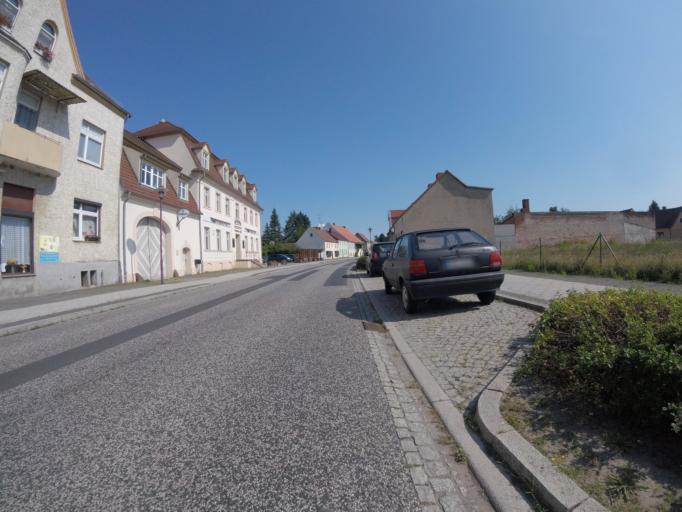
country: DE
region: Brandenburg
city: Mullrose
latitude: 52.2490
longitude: 14.4182
